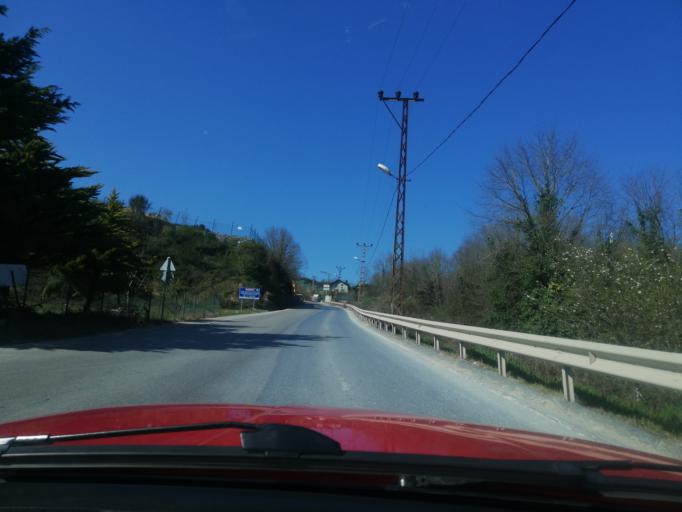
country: TR
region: Istanbul
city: Mahmut Sevket Pasa
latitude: 41.1012
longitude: 29.1589
